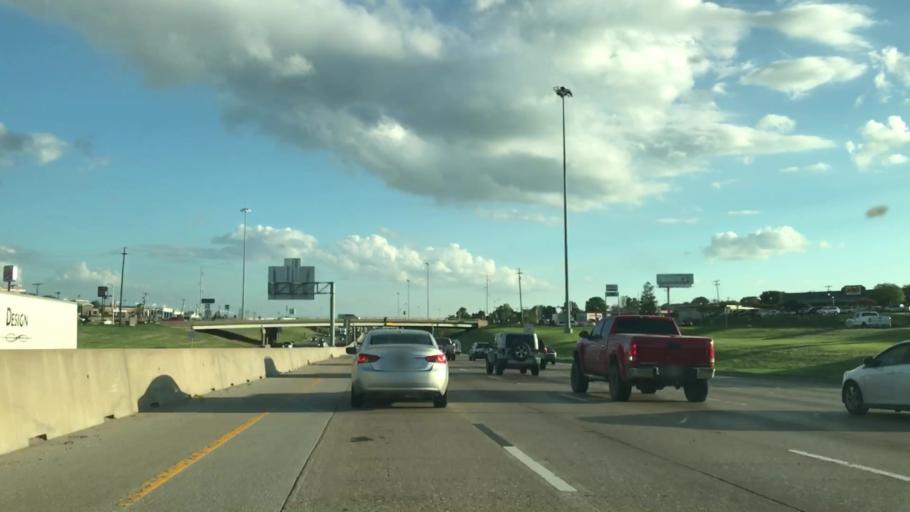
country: US
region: Texas
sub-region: Dallas County
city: Garland
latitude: 32.8374
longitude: -96.6329
